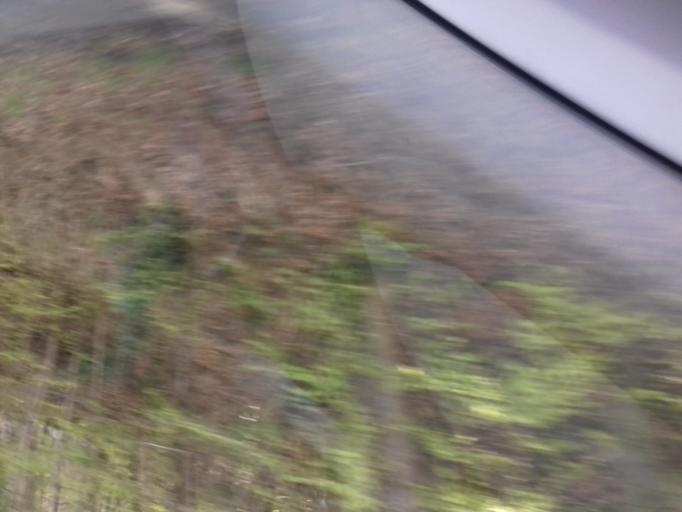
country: GB
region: Northern Ireland
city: Irvinestown
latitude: 54.4181
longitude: -7.7330
